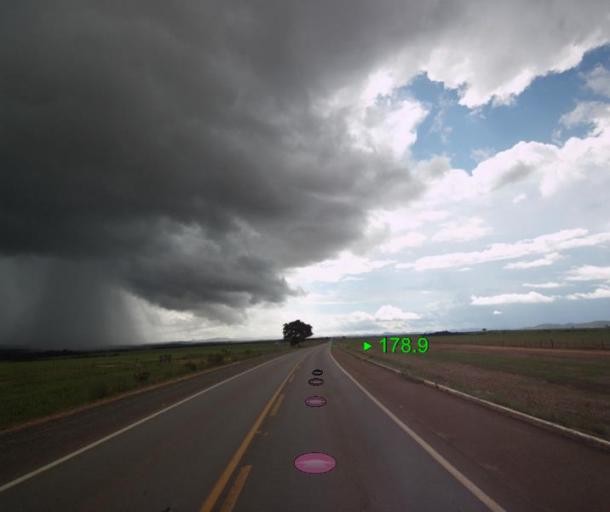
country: BR
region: Goias
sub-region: Uruacu
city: Uruacu
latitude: -14.6537
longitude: -49.1649
